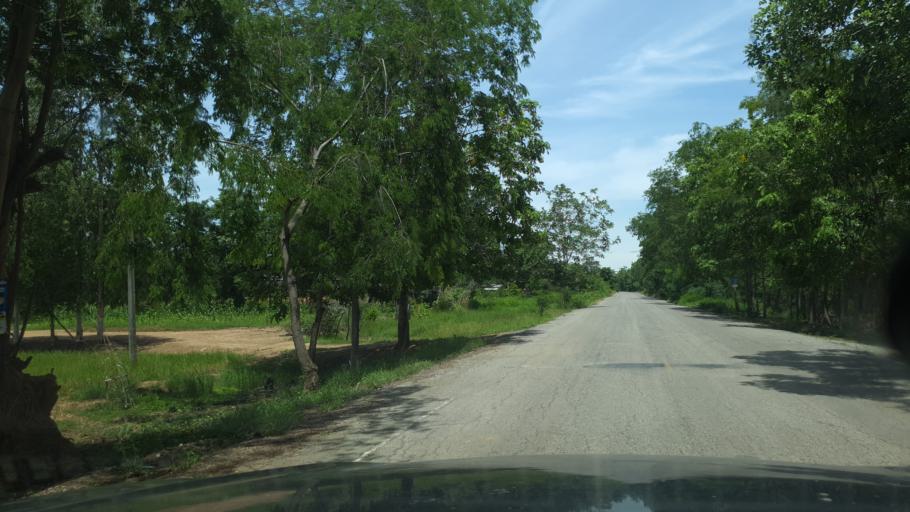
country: TH
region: Sukhothai
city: Ban Na
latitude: 17.0938
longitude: 99.6829
